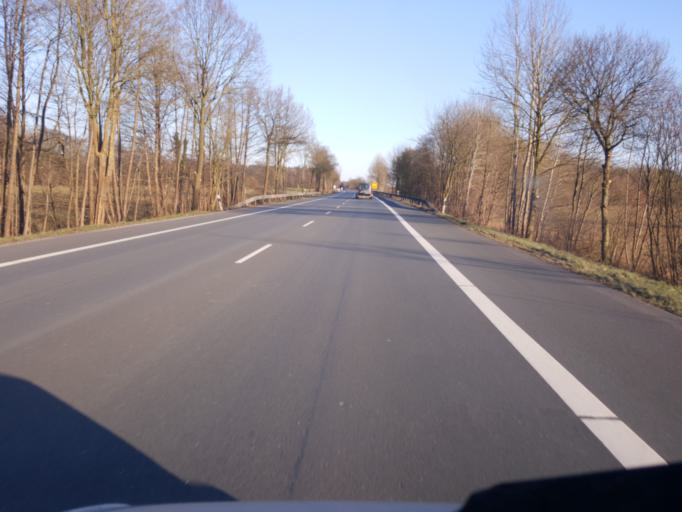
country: DE
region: North Rhine-Westphalia
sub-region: Regierungsbezirk Detmold
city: Hille
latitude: 52.3898
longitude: 8.7181
